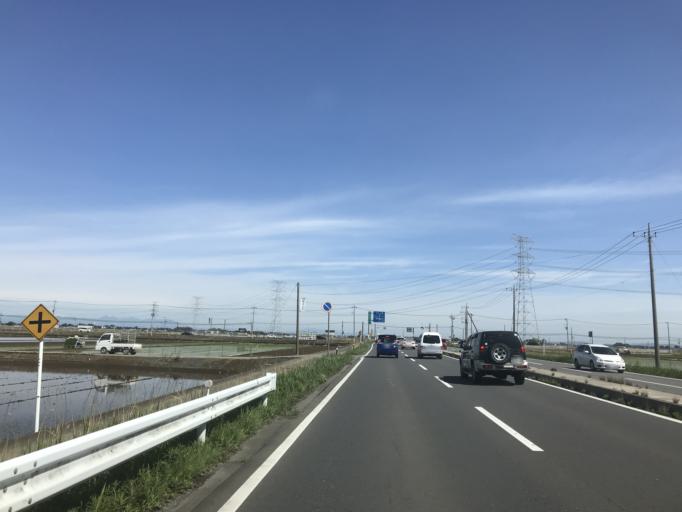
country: JP
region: Ibaraki
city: Ishige
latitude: 36.1198
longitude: 139.9827
